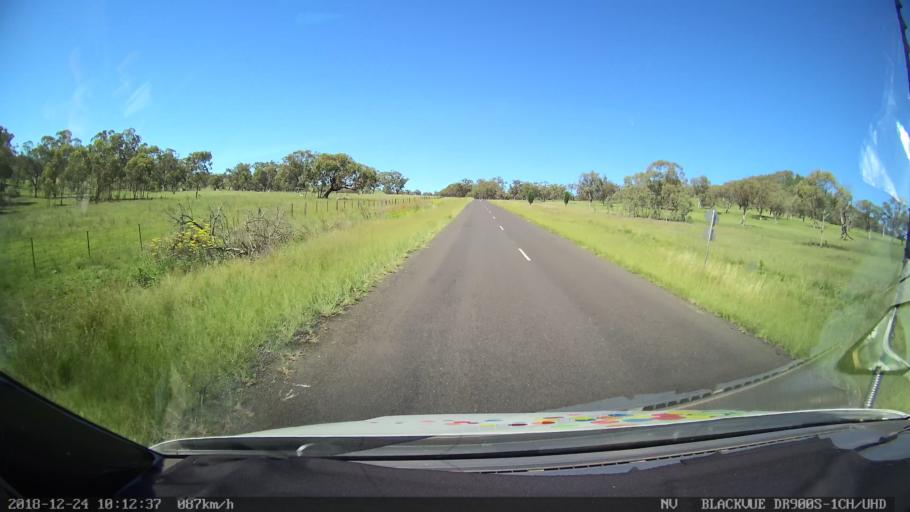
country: AU
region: New South Wales
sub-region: Liverpool Plains
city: Quirindi
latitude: -31.6809
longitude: 150.6462
